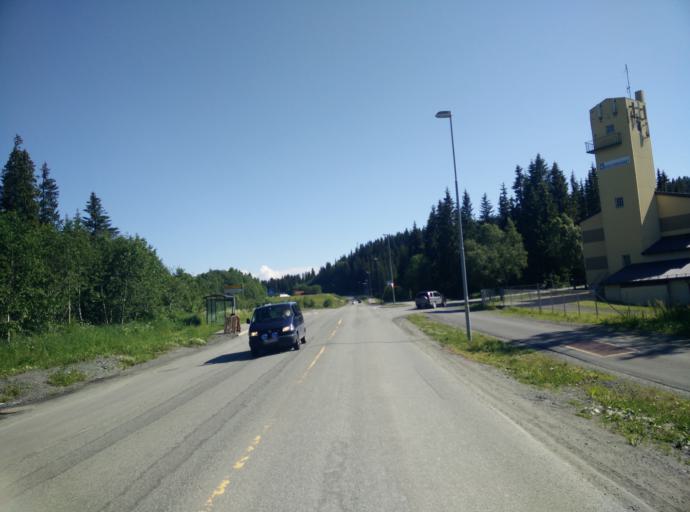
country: NO
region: Sor-Trondelag
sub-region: Trondheim
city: Trondheim
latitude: 63.3798
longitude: 10.3160
